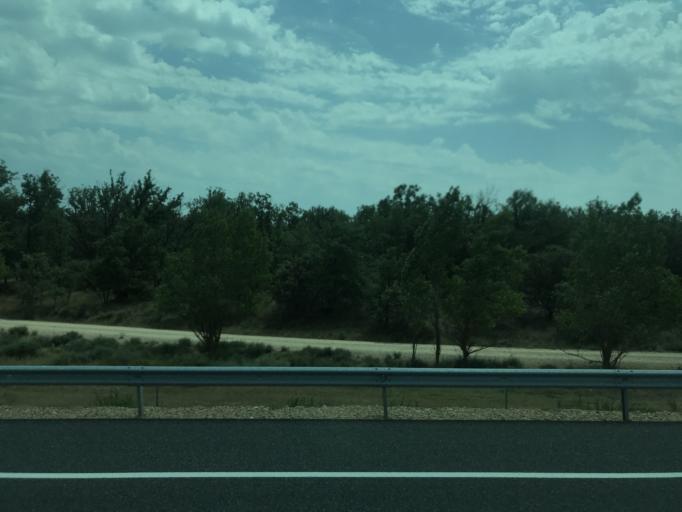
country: ES
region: Castille and Leon
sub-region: Provincia de Burgos
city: Madrigalejo del Monte
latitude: 42.0958
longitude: -3.7252
